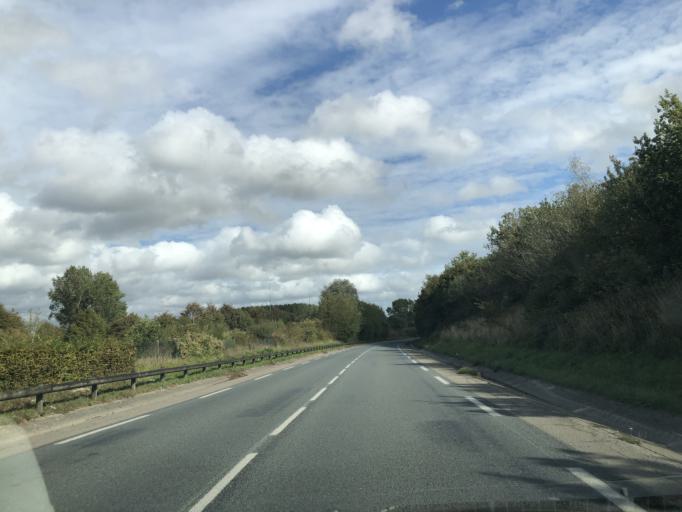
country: FR
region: Nord-Pas-de-Calais
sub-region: Departement du Pas-de-Calais
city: Hallines
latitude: 50.7060
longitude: 2.2324
